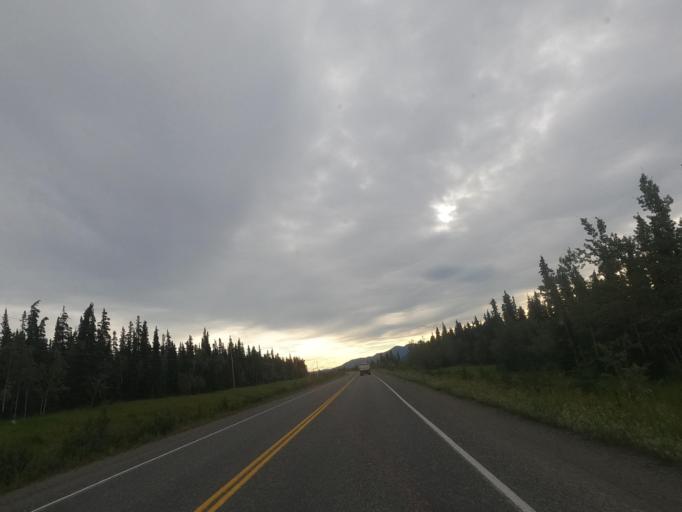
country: CA
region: Yukon
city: Whitehorse
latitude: 60.7657
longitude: -136.0929
